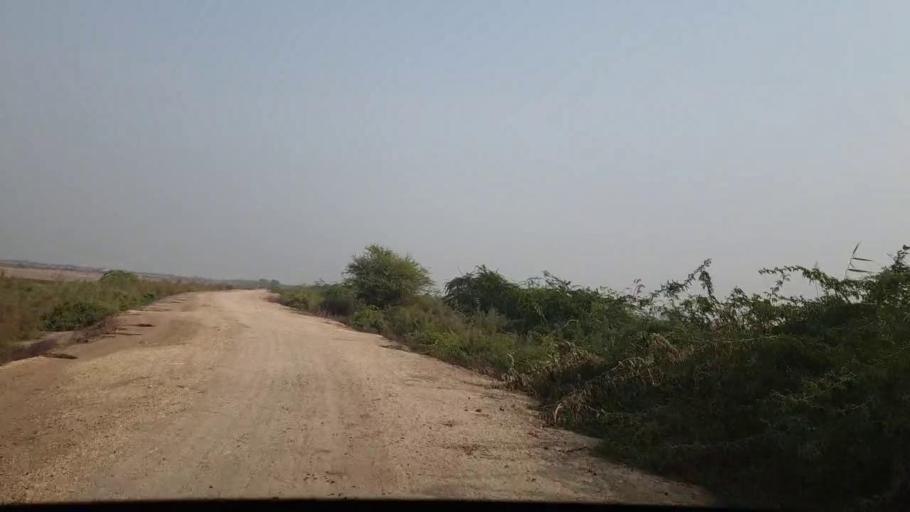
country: PK
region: Sindh
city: Jati
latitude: 24.2796
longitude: 68.4199
